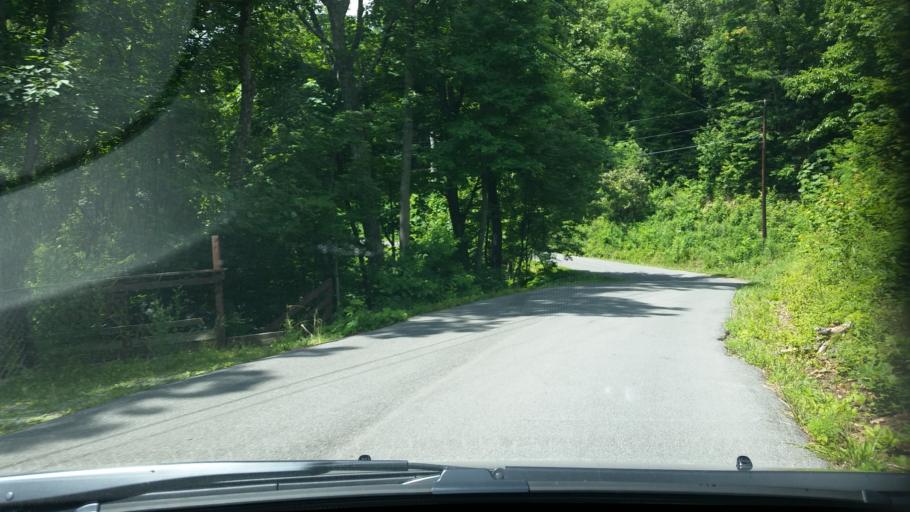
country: US
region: Tennessee
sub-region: Sevier County
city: Gatlinburg
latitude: 35.7122
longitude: -83.5498
